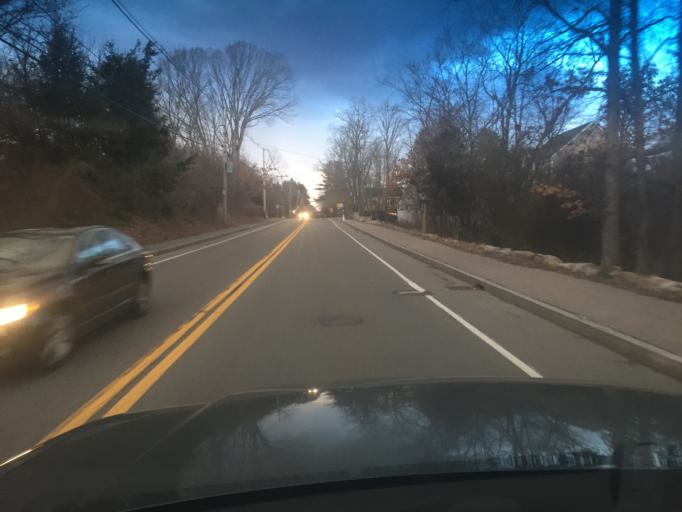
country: US
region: Massachusetts
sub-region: Middlesex County
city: Holliston
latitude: 42.1569
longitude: -71.4435
